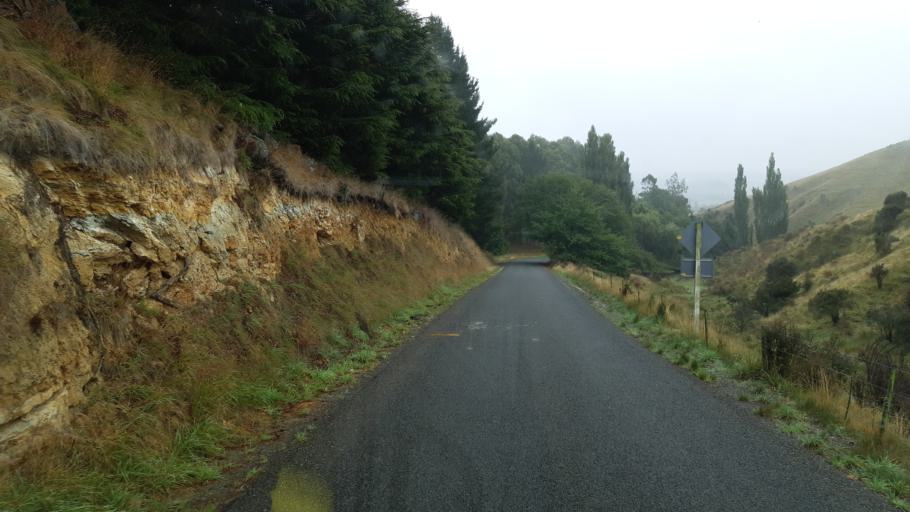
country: NZ
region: Otago
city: Oamaru
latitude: -44.9400
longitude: 170.6179
